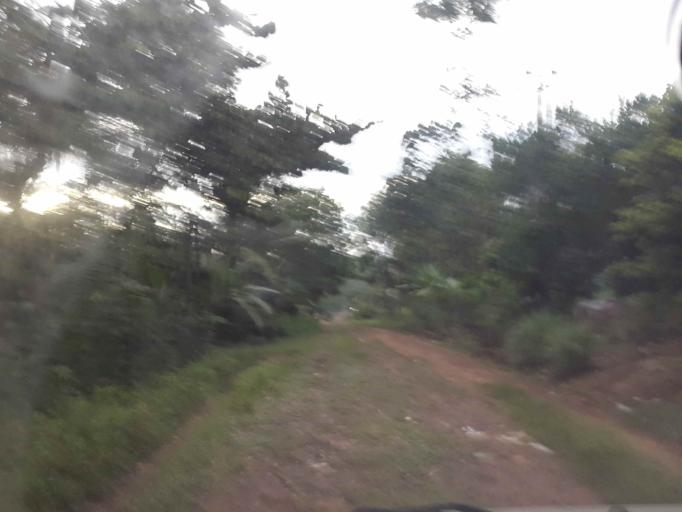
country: ID
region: Lampung
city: Sidorejo
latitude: -5.5568
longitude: 105.5336
